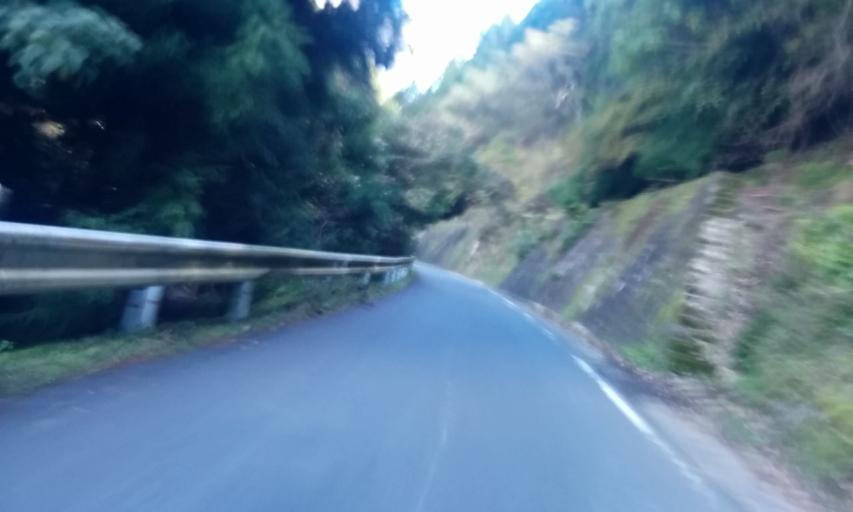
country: JP
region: Kyoto
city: Kameoka
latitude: 35.1291
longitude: 135.5707
